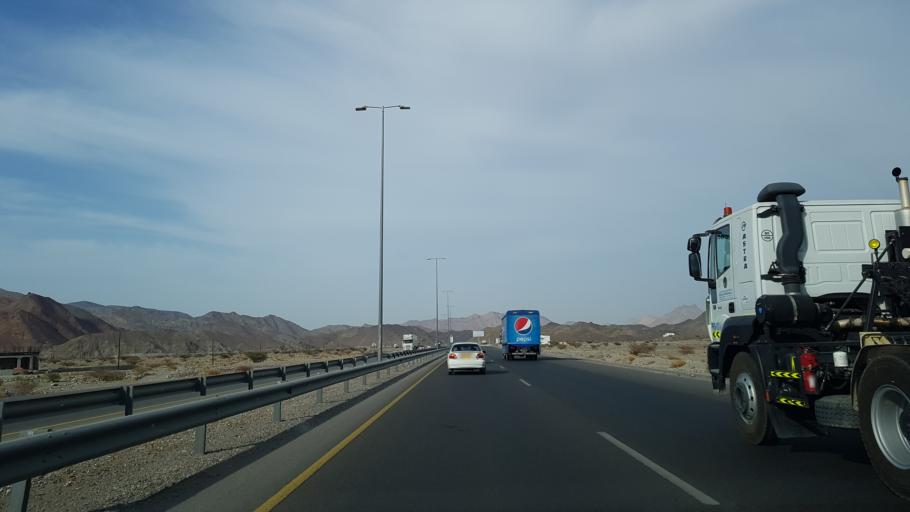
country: OM
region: Muhafazat ad Dakhiliyah
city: Sufalat Sama'il
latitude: 23.3806
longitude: 58.0538
